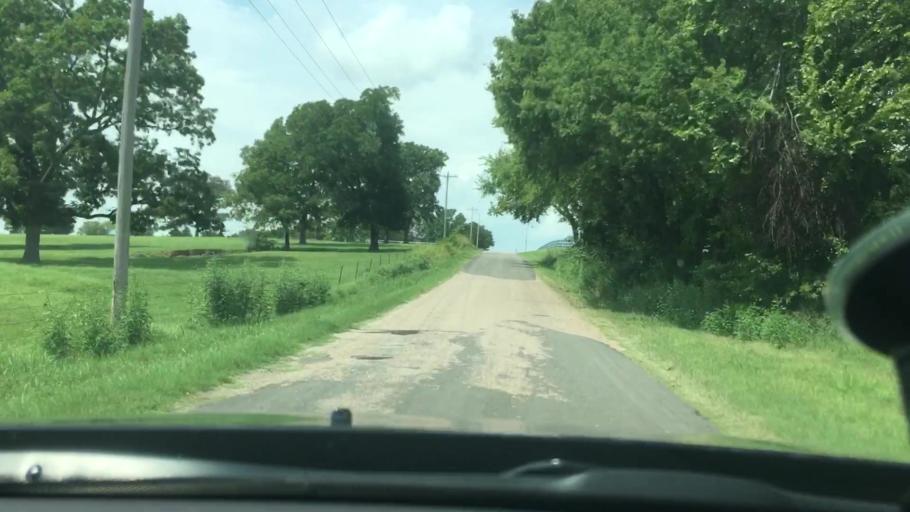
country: US
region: Oklahoma
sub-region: Carter County
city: Dickson
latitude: 34.2308
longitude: -96.9127
